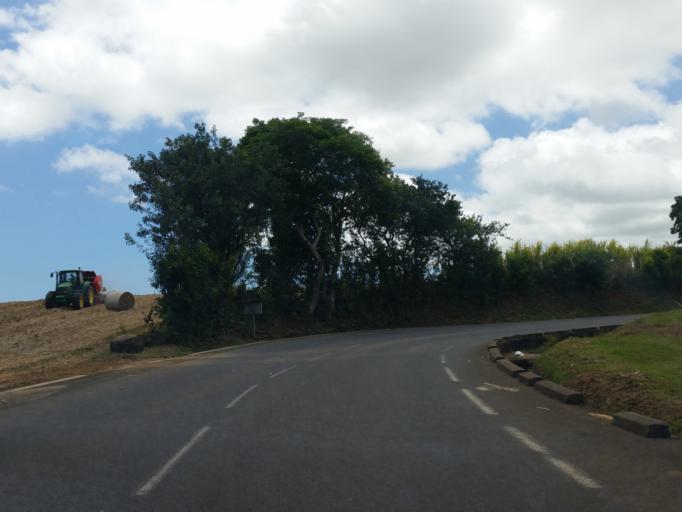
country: RE
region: Reunion
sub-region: Reunion
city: Sainte-Marie
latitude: -20.9158
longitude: 55.5368
